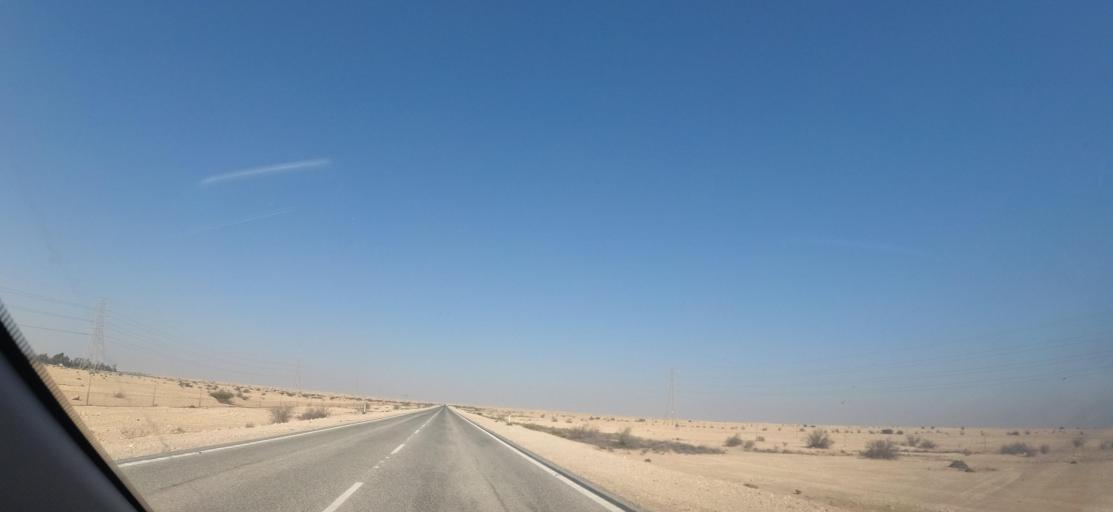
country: QA
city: Al Jumayliyah
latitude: 25.6662
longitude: 51.1244
